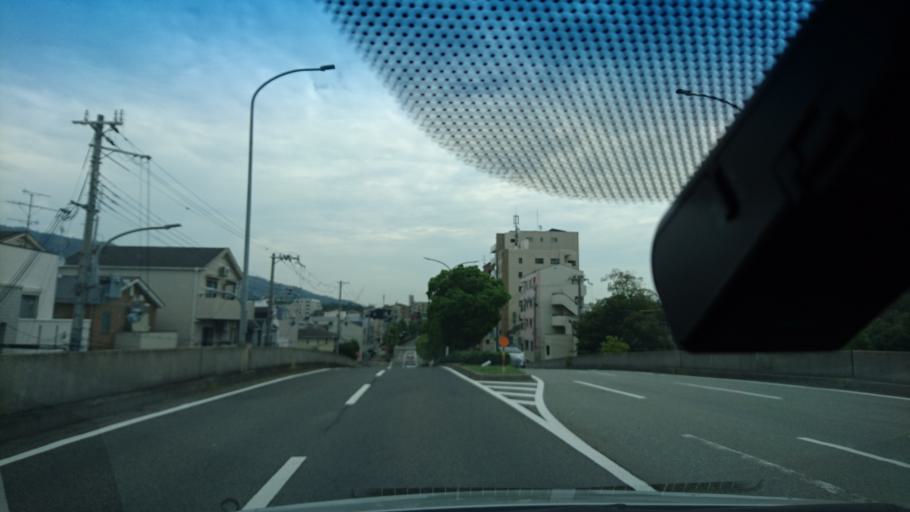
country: JP
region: Hyogo
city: Ashiya
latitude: 34.7202
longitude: 135.2476
